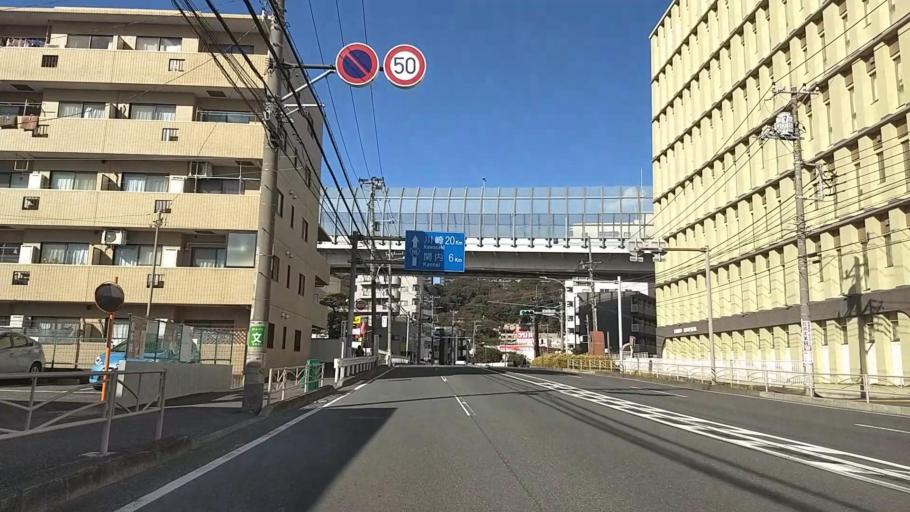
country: JP
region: Kanagawa
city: Yokohama
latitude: 35.3960
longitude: 139.6141
